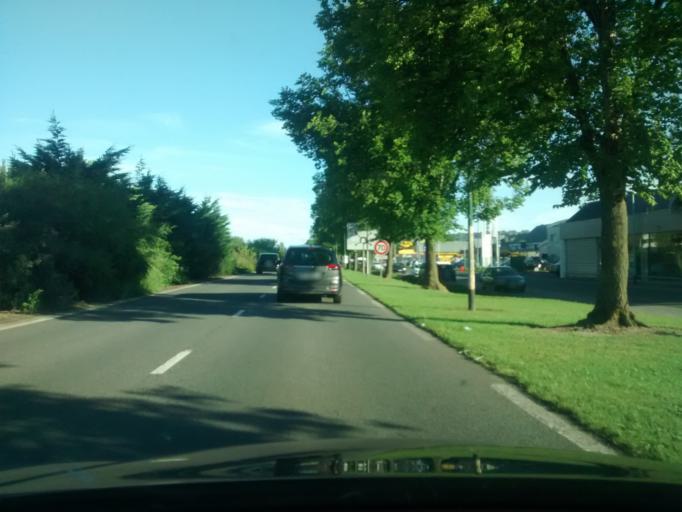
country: FR
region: Lower Normandy
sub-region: Departement du Calvados
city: Touques
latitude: 49.3446
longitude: 0.0994
